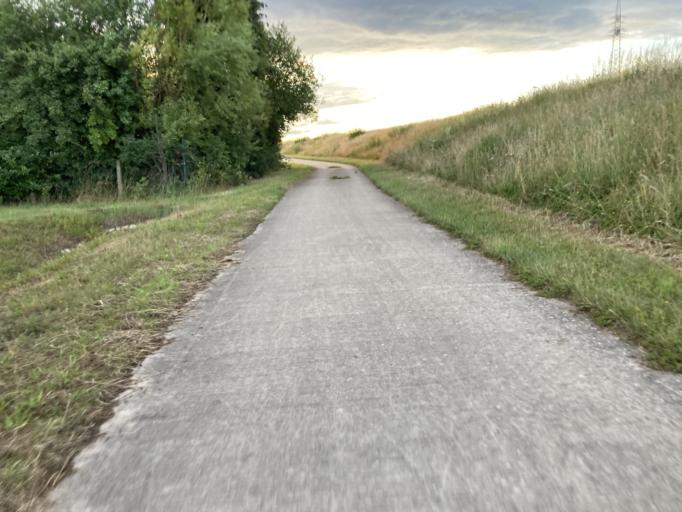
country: DE
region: Lower Saxony
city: Verden
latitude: 52.9255
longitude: 9.2164
